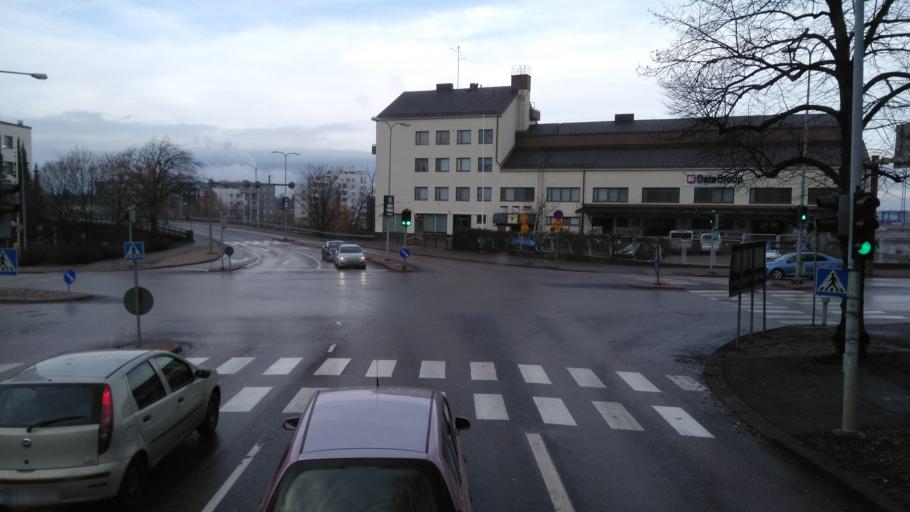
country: FI
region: Kymenlaakso
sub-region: Kotka-Hamina
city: Kotka
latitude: 60.4648
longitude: 26.9346
